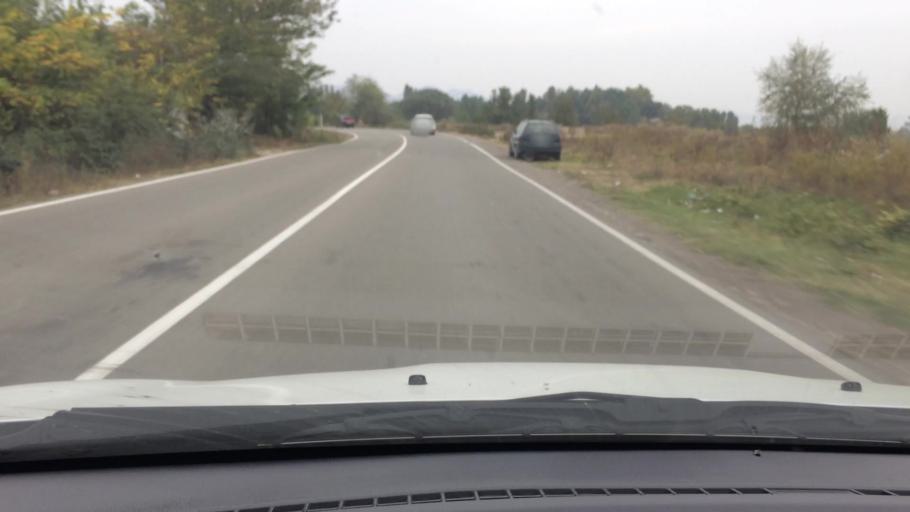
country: AM
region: Tavush
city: Bagratashen
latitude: 41.2570
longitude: 44.7977
